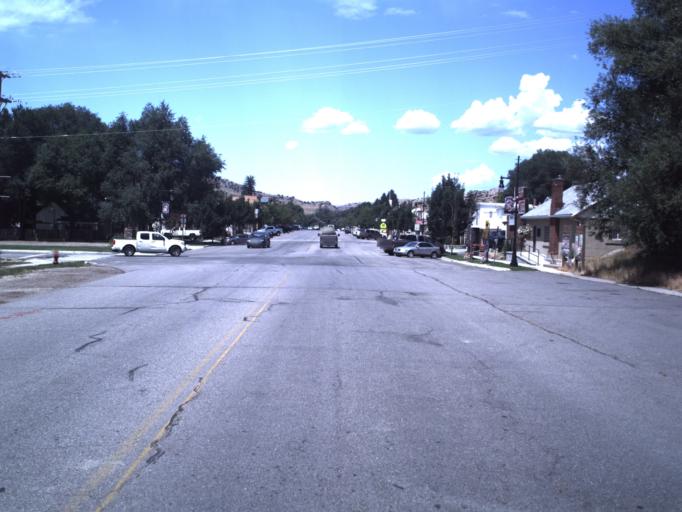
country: US
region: Utah
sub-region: Summit County
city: Coalville
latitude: 40.9136
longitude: -111.3969
